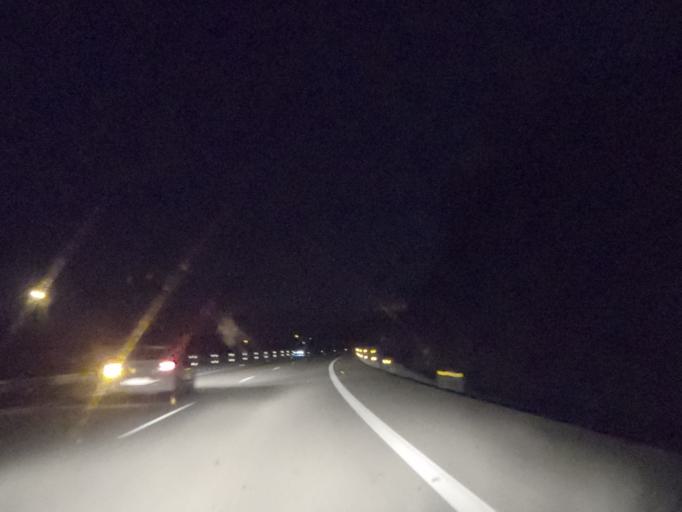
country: ES
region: Galicia
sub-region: Provincia da Coruna
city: Oroso
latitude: 42.9606
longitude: -8.4565
